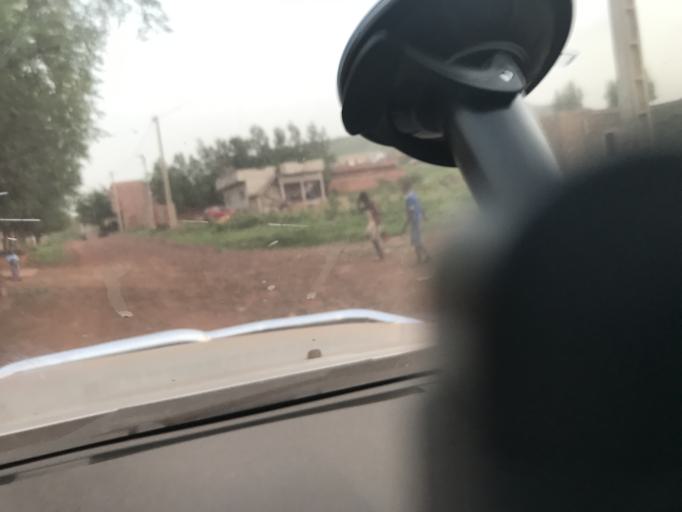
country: ML
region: Bamako
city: Bamako
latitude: 12.6504
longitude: -7.8819
